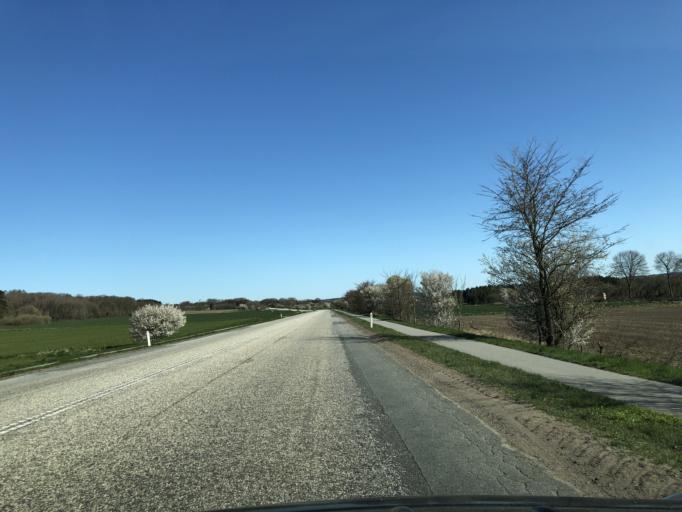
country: DK
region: North Denmark
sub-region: Rebild Kommune
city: Stovring
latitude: 56.9172
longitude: 9.8560
